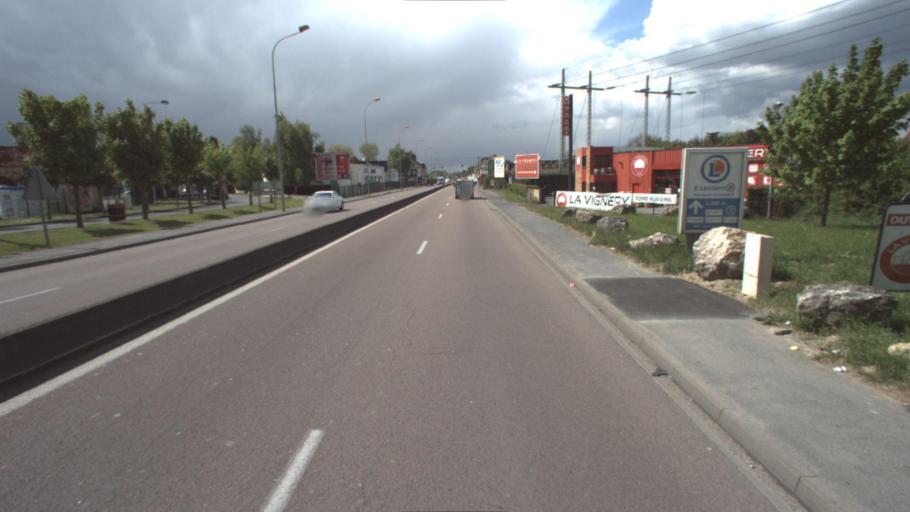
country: FR
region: Ile-de-France
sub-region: Departement du Val-de-Marne
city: La Queue-en-Brie
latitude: 48.7760
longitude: 2.6008
